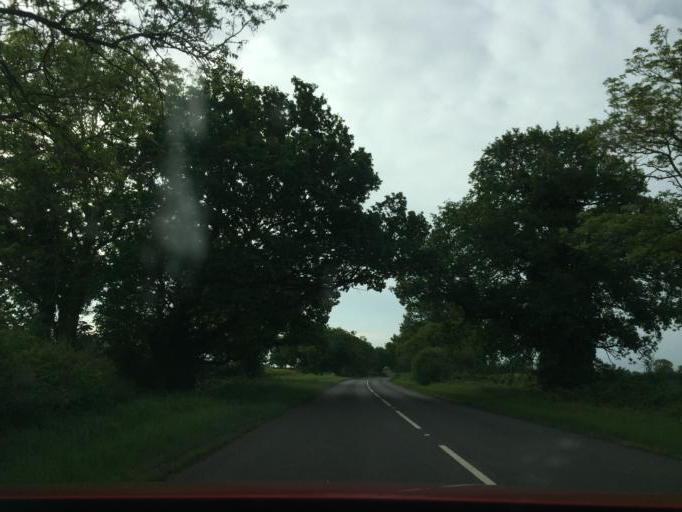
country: GB
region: England
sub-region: Leicestershire
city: Hinckley
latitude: 52.4801
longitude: -1.3308
